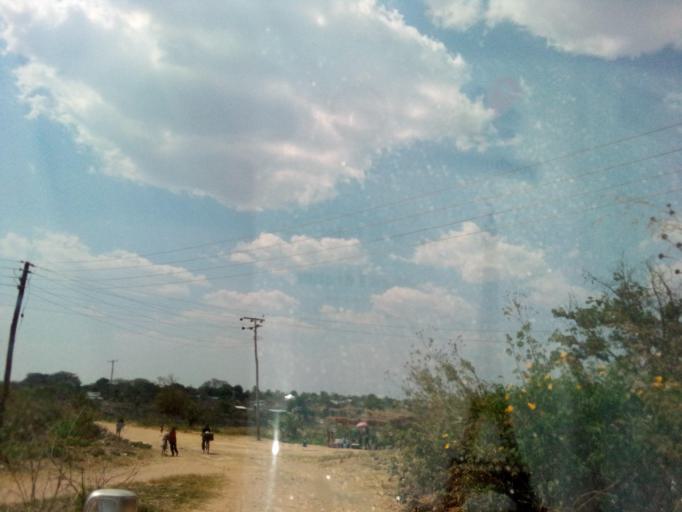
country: ZM
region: Northern
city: Mpika
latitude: -11.8463
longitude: 31.3894
